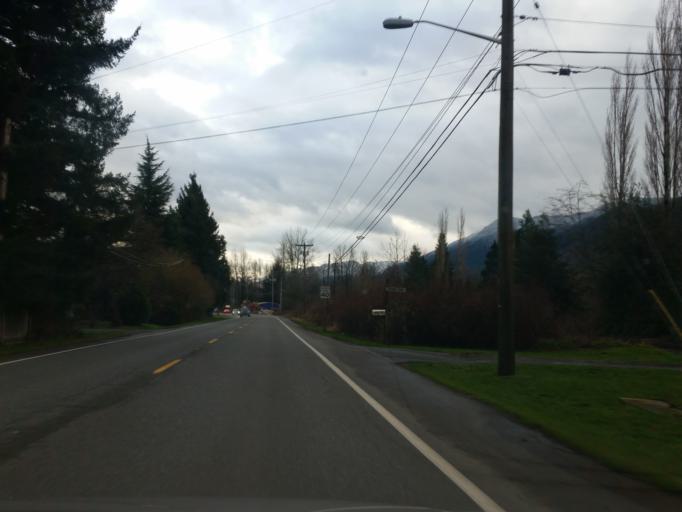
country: US
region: Washington
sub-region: King County
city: Snoqualmie
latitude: 47.5217
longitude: -121.8202
